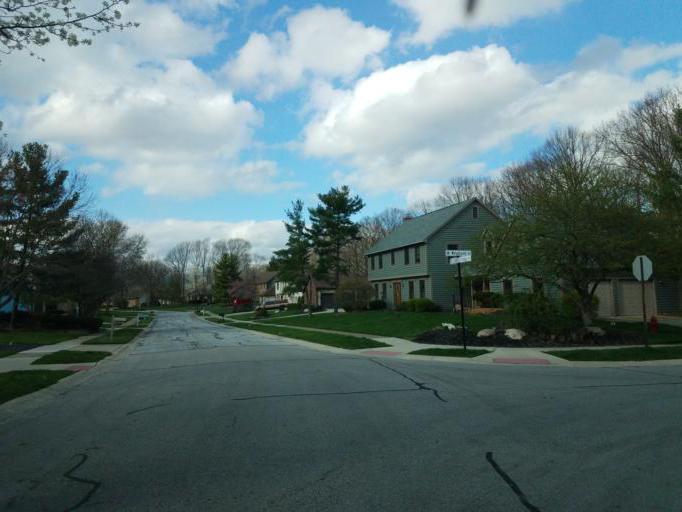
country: US
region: Ohio
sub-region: Delaware County
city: Powell
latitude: 40.1615
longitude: -83.0647
